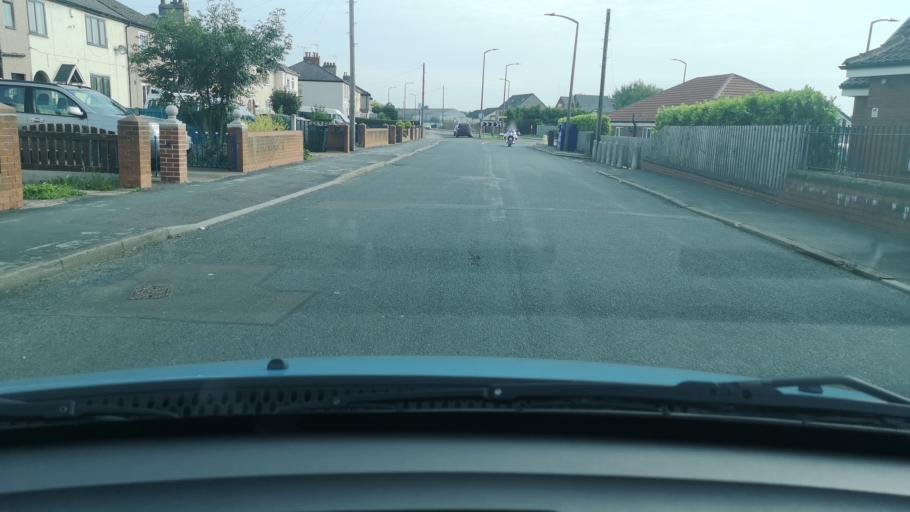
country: GB
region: England
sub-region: Doncaster
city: Askern
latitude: 53.6100
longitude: -1.1552
